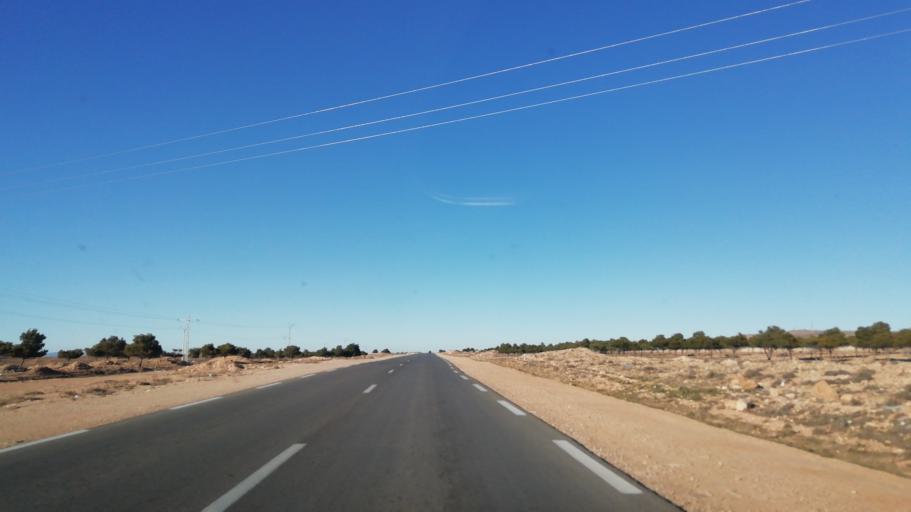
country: DZ
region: Tlemcen
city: Sebdou
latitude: 34.2438
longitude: -1.2570
